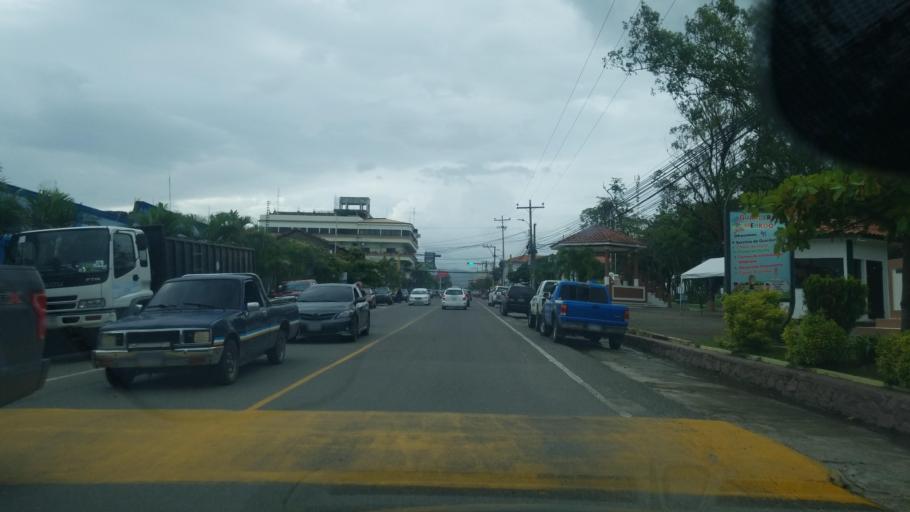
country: HN
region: Ocotepeque
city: Nueva Ocotepeque
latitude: 14.4339
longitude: -89.1828
